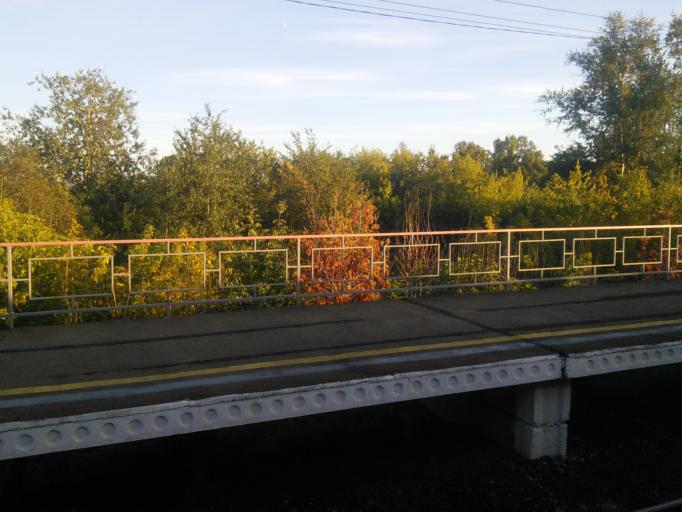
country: RU
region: Moskovskaya
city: Pavlovskiy Posad
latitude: 55.7695
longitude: 38.6306
